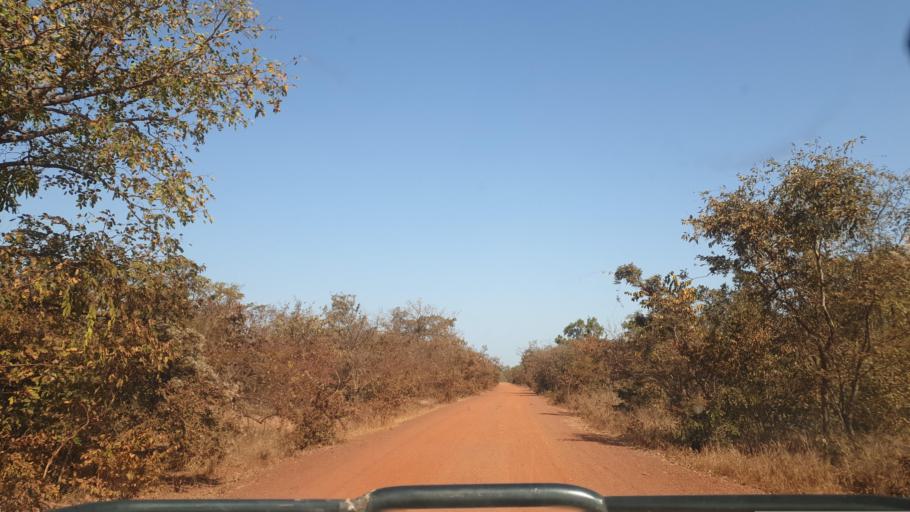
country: ML
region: Koulikoro
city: Dioila
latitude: 11.8492
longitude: -6.9788
